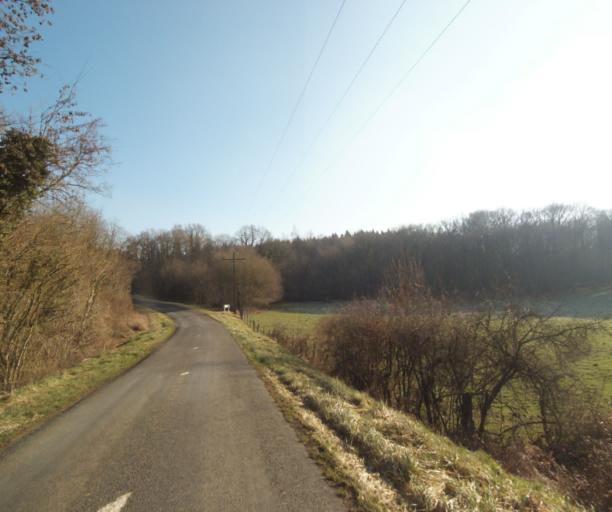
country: FR
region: Champagne-Ardenne
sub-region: Departement de la Haute-Marne
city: Bienville
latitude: 48.4999
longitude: 5.0467
